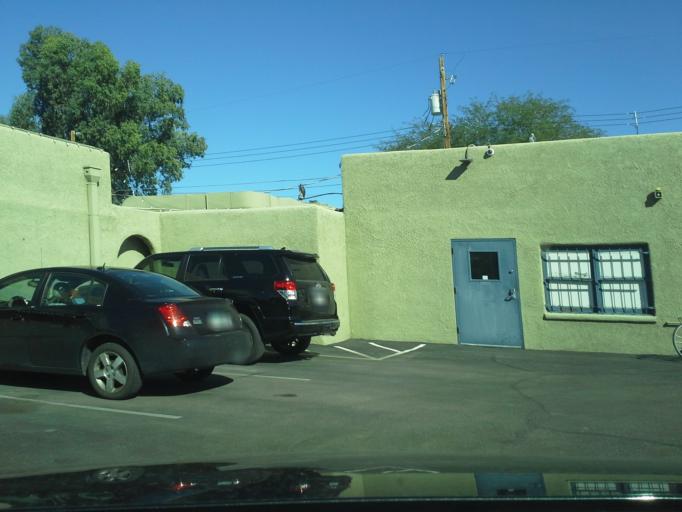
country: US
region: Arizona
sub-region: Pima County
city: Tucson
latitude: 32.2543
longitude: -110.9436
